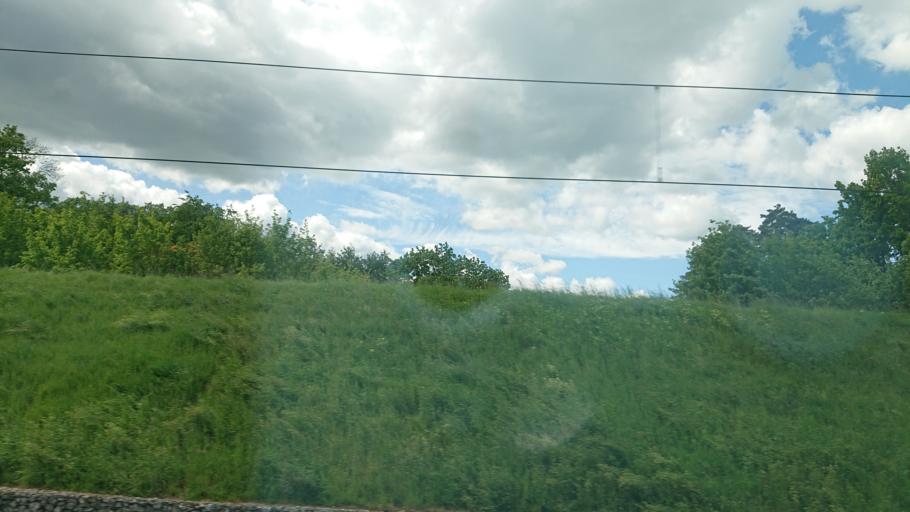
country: CH
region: Geneva
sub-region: Geneva
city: Bellevue
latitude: 46.2539
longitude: 6.1488
